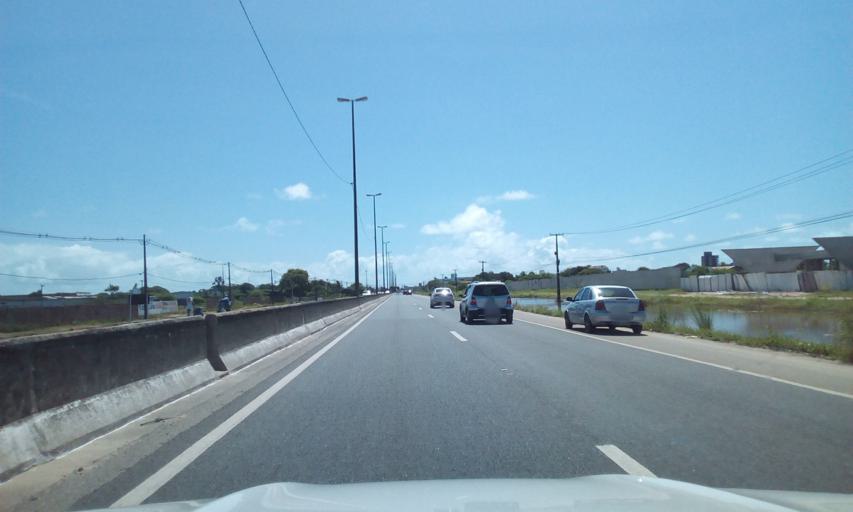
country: BR
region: Paraiba
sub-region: Cabedelo
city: Cabedelo
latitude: -7.0268
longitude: -34.8388
